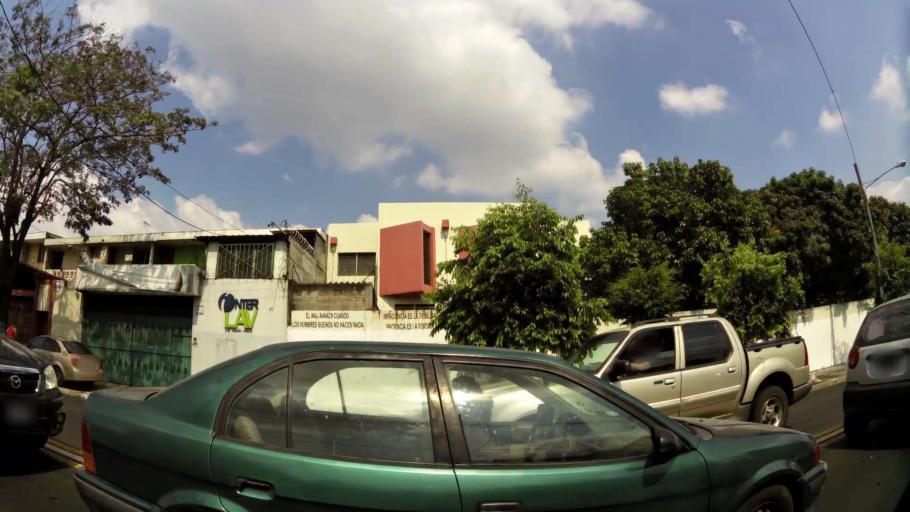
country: SV
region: San Salvador
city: Mejicanos
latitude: 13.7166
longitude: -89.2184
